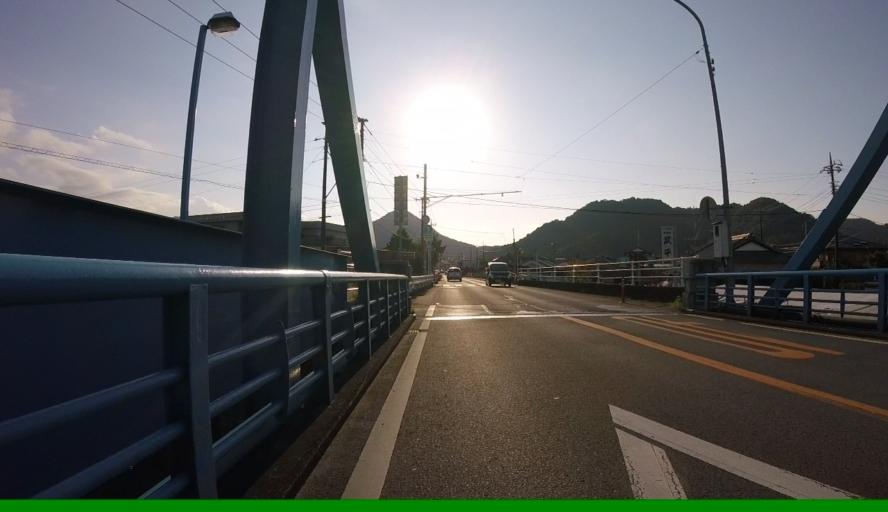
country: JP
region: Shizuoka
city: Mishima
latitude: 35.0915
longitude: 138.9012
